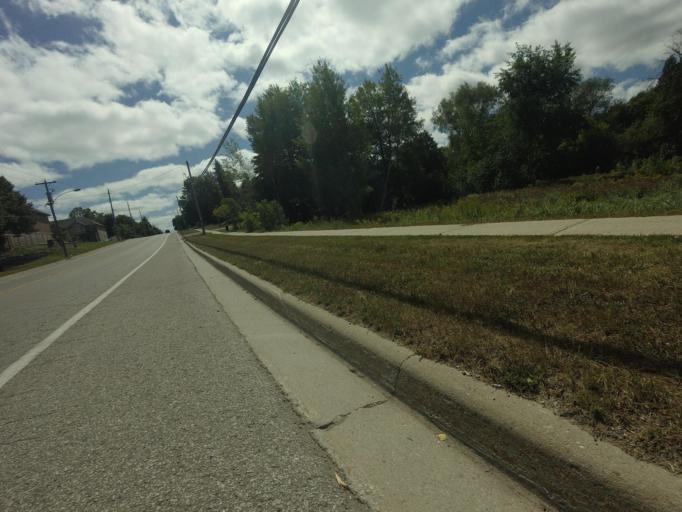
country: CA
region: Ontario
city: Uxbridge
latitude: 44.1184
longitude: -79.1246
